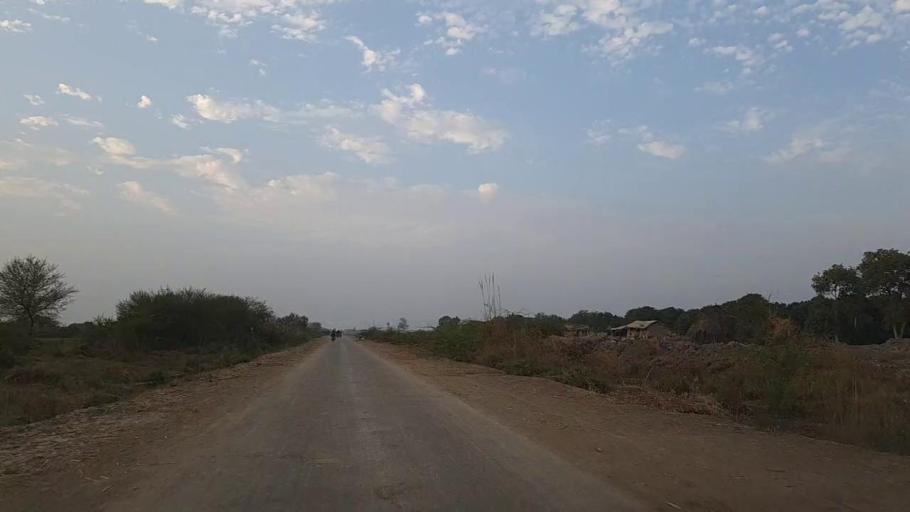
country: PK
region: Sindh
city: Mirwah Gorchani
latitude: 25.3238
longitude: 69.2177
